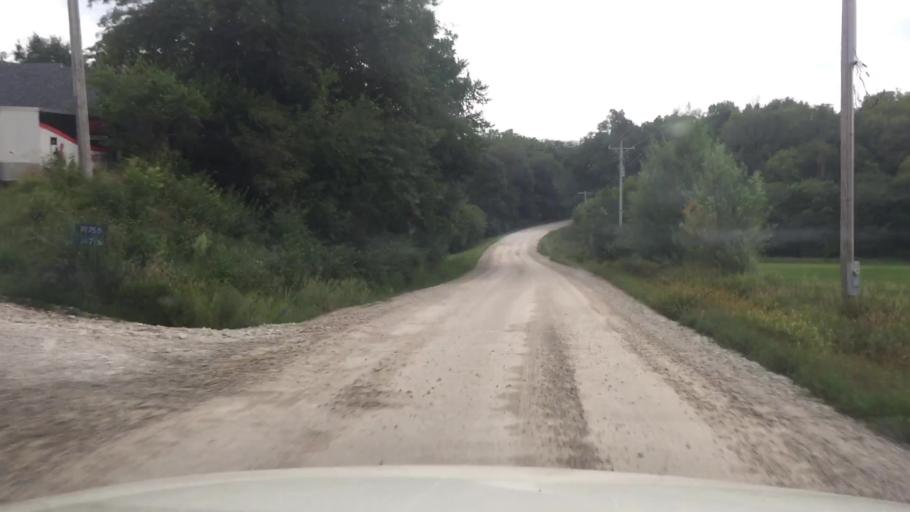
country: US
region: Iowa
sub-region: Story County
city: Huxley
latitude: 41.9107
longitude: -93.5746
